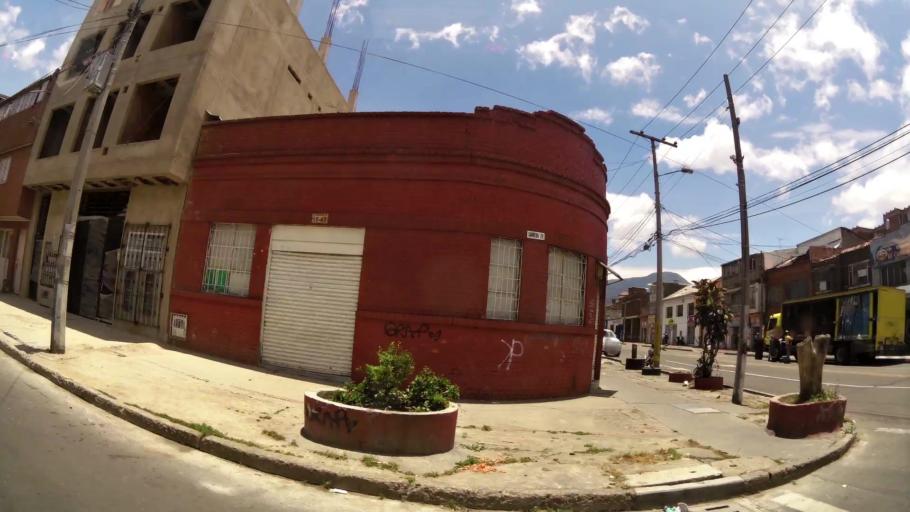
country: CO
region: Bogota D.C.
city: Bogota
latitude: 4.5896
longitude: -74.0983
